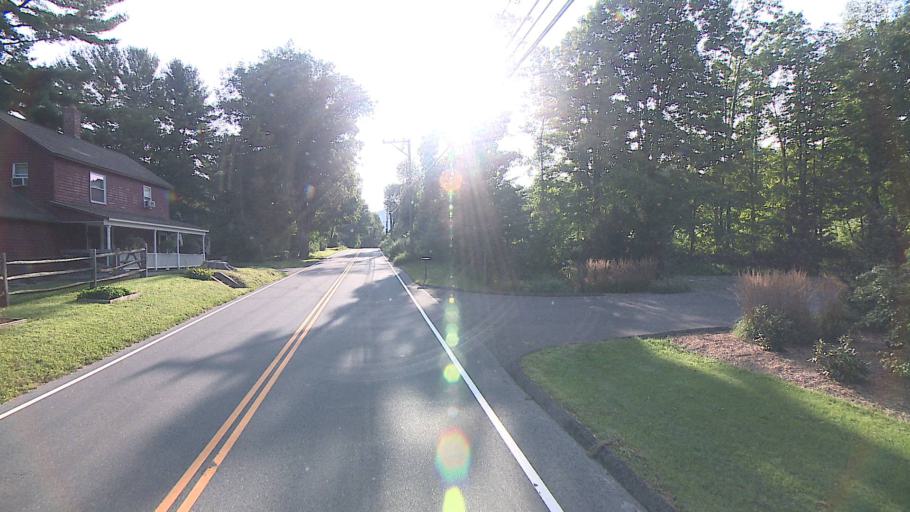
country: US
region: Connecticut
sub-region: Litchfield County
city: Kent
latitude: 41.7400
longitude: -73.4632
